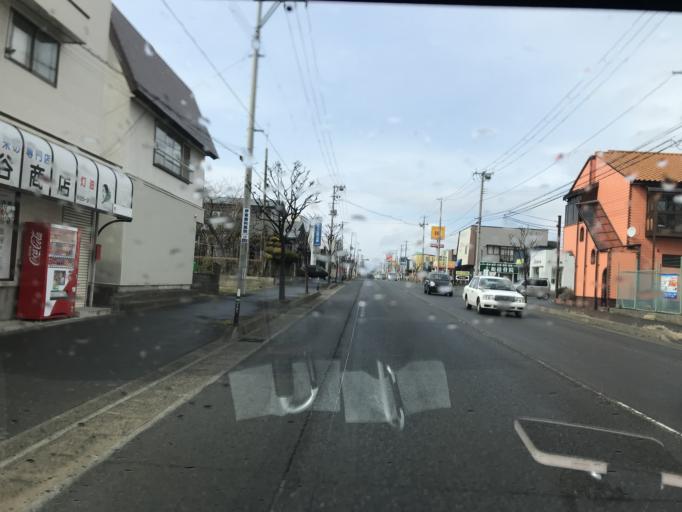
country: JP
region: Iwate
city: Kitakami
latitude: 39.3015
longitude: 141.1169
